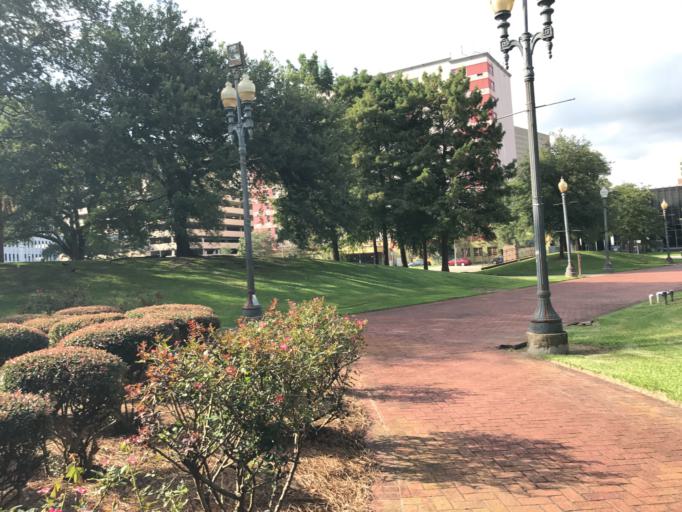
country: US
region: Louisiana
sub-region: Orleans Parish
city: New Orleans
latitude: 29.9530
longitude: -90.0762
